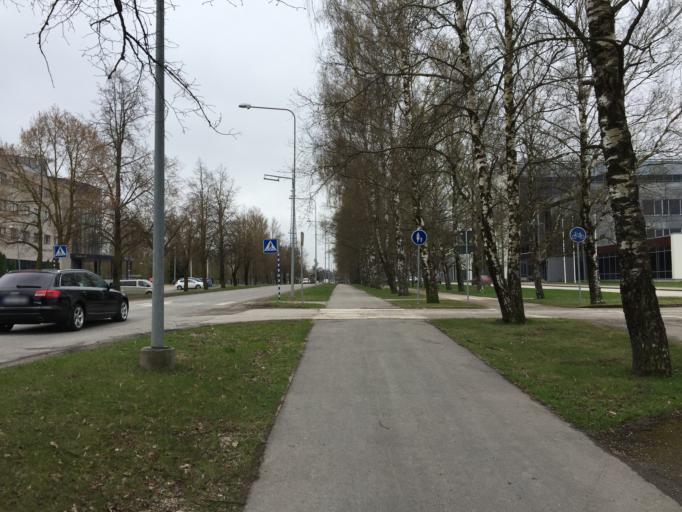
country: EE
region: Tartu
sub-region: Tartu linn
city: Tartu
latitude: 58.3686
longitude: 26.6923
